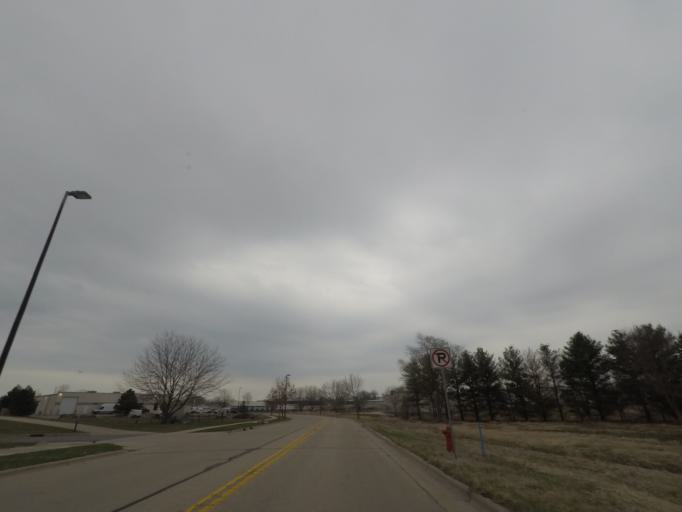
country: US
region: Wisconsin
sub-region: Dane County
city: Middleton
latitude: 43.1040
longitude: -89.5387
